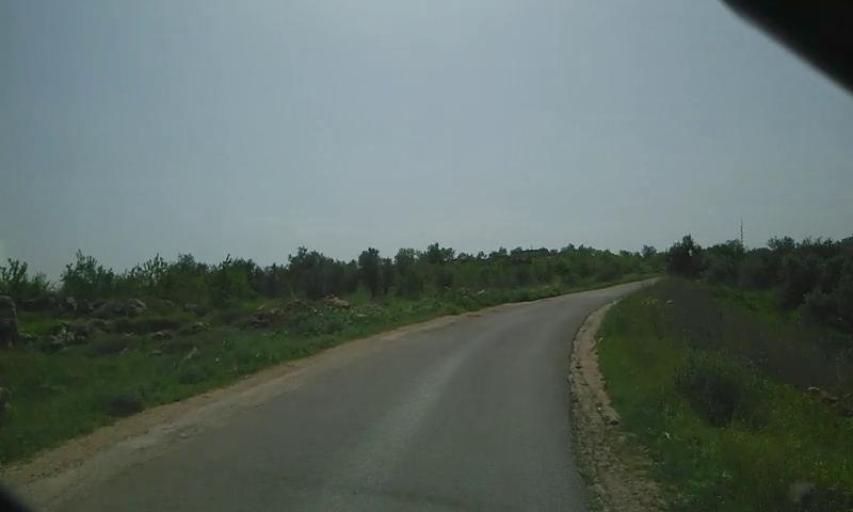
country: PS
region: West Bank
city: At Taybah
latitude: 32.4995
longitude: 35.1965
